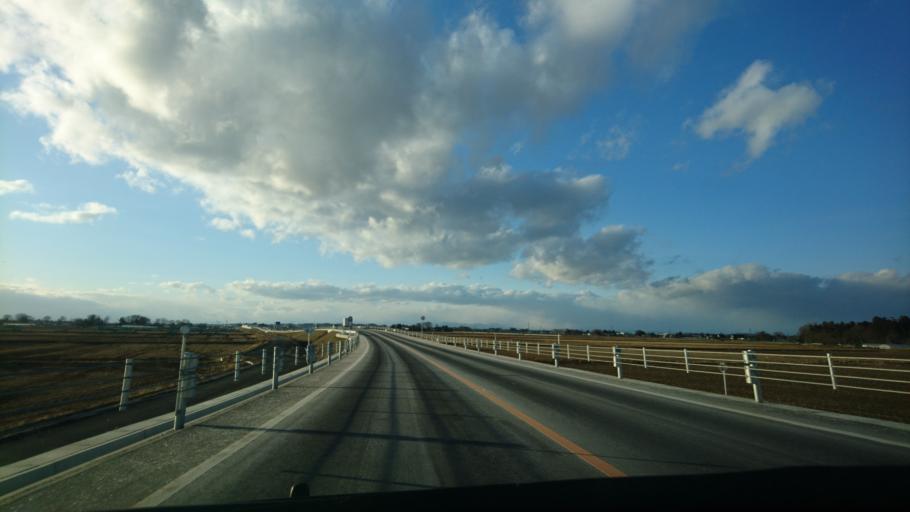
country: JP
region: Miyagi
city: Wakuya
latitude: 38.6848
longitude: 141.2478
